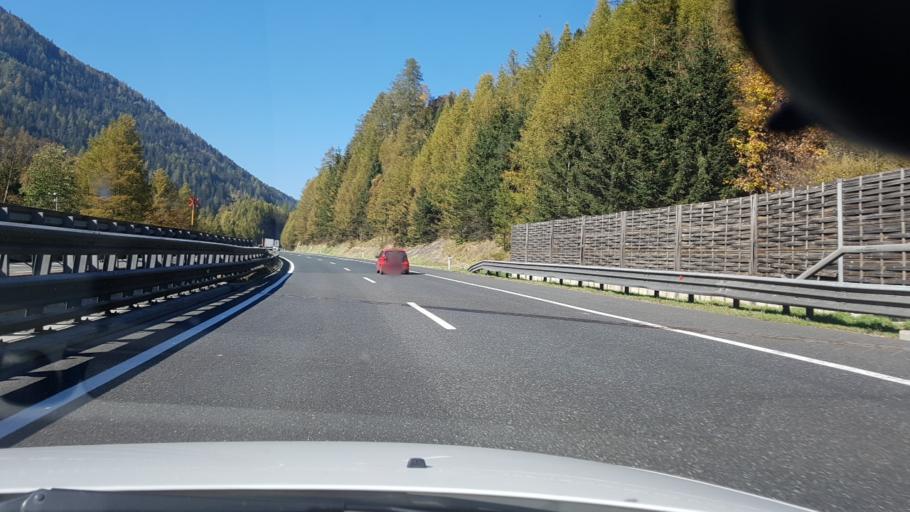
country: AT
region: Salzburg
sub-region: Politischer Bezirk Tamsweg
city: Zederhaus
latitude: 47.1407
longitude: 13.5300
